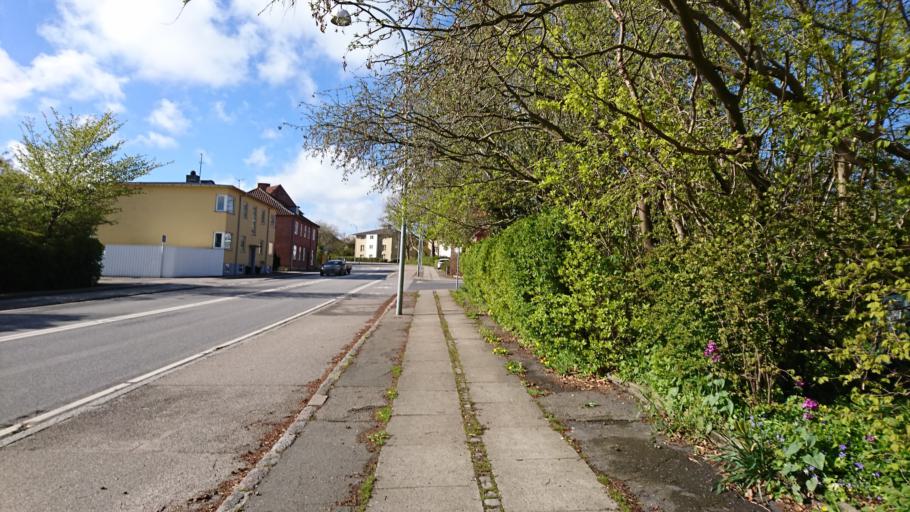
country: DK
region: Zealand
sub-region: Roskilde Kommune
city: Roskilde
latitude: 55.6416
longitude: 12.0724
